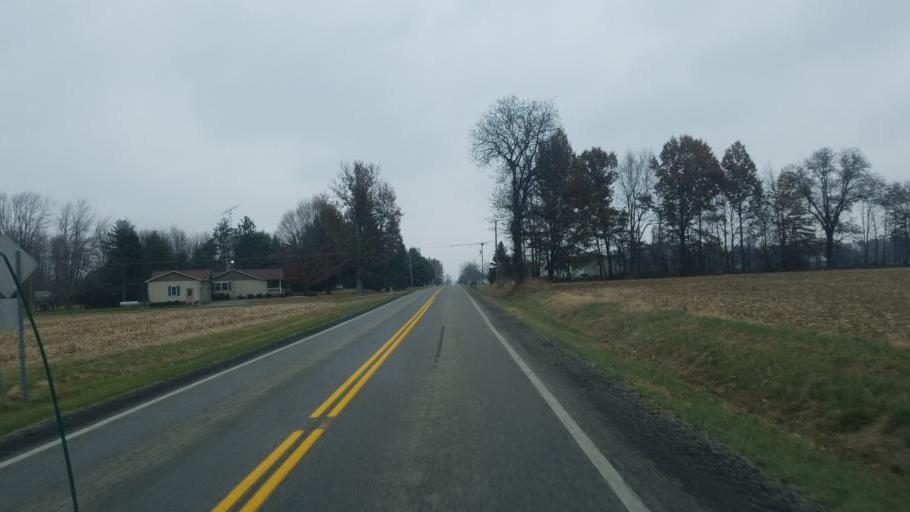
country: US
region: Ohio
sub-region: Crawford County
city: Crestline
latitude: 40.8240
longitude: -82.7912
